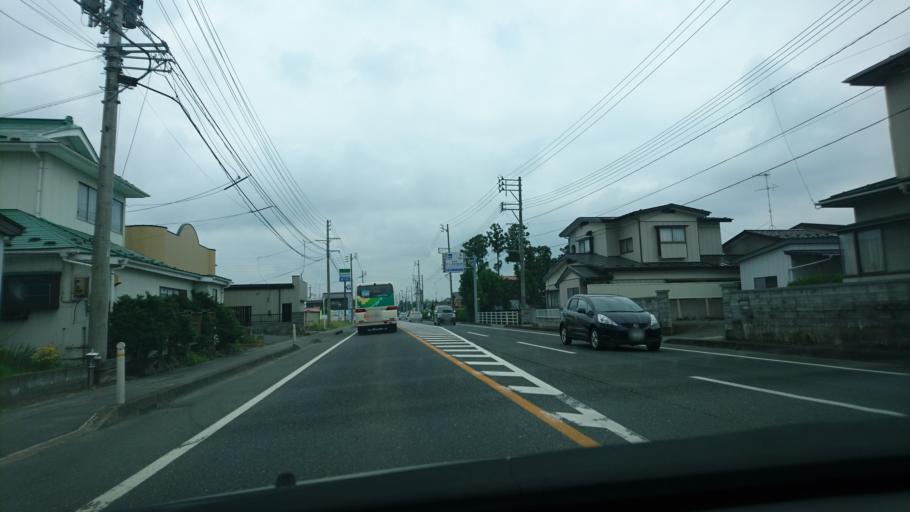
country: JP
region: Miyagi
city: Furukawa
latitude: 38.7098
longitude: 140.8325
